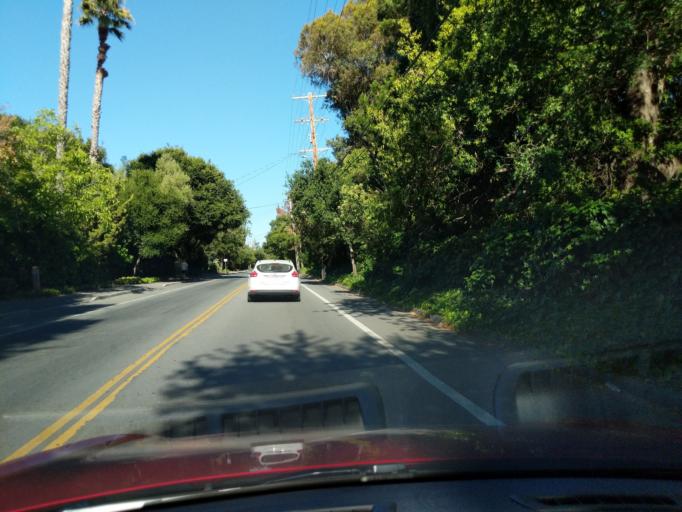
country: US
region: California
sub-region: San Mateo County
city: North Fair Oaks
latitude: 37.4766
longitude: -122.1857
